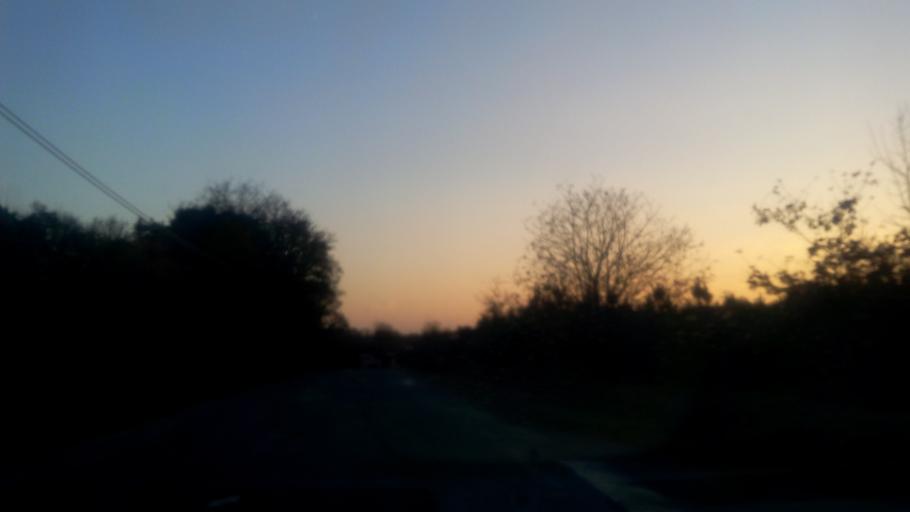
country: FR
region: Brittany
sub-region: Departement d'Ille-et-Vilaine
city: Bains-sur-Oust
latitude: 47.7235
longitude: -2.0537
